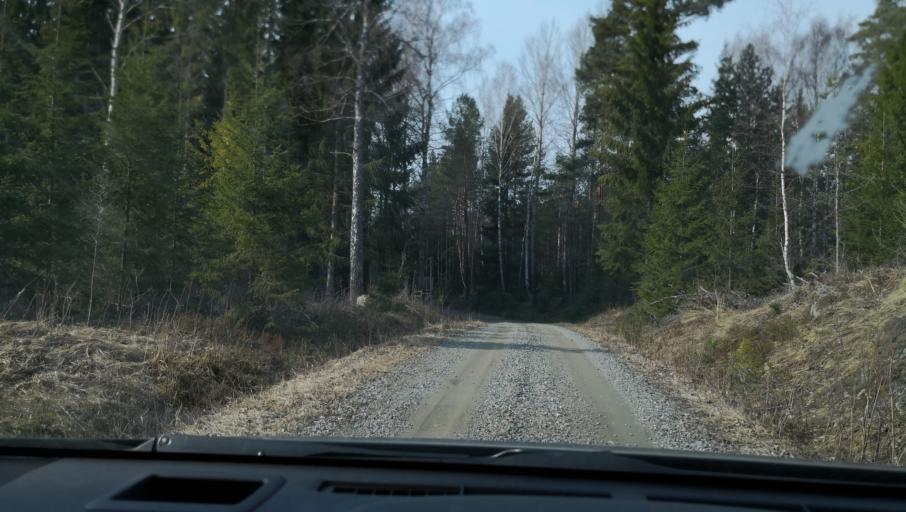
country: SE
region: OErebro
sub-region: Lindesbergs Kommun
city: Frovi
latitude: 59.3849
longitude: 15.4081
